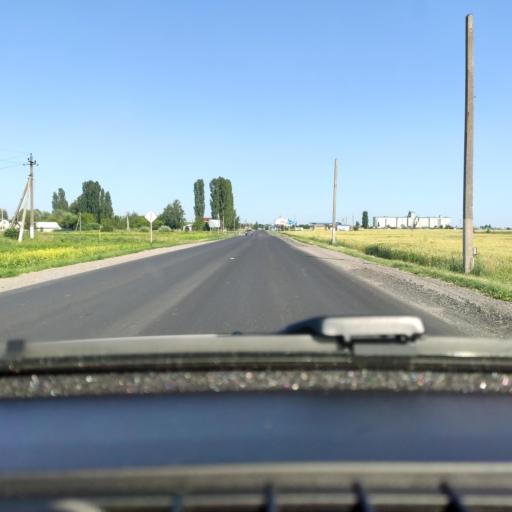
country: RU
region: Voronezj
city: Panino
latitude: 51.6492
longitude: 40.1087
